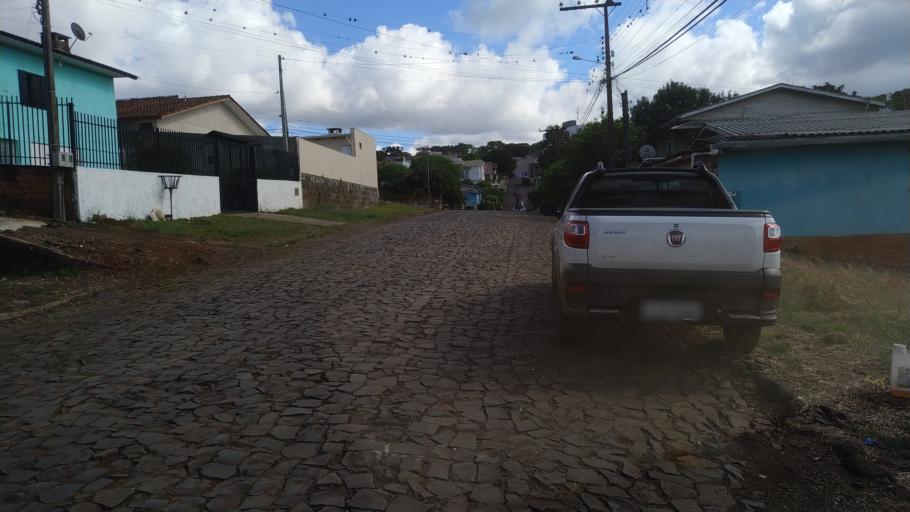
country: BR
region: Santa Catarina
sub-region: Chapeco
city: Chapeco
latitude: -27.1017
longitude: -52.6370
